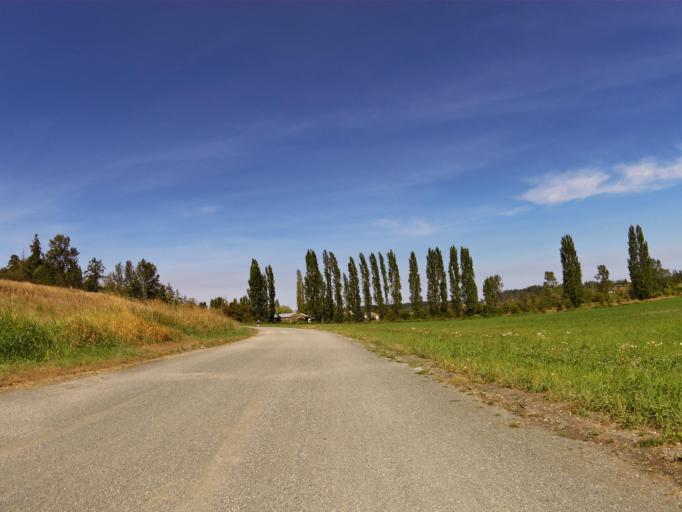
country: CA
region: British Columbia
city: North Saanich
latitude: 48.5564
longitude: -123.3865
